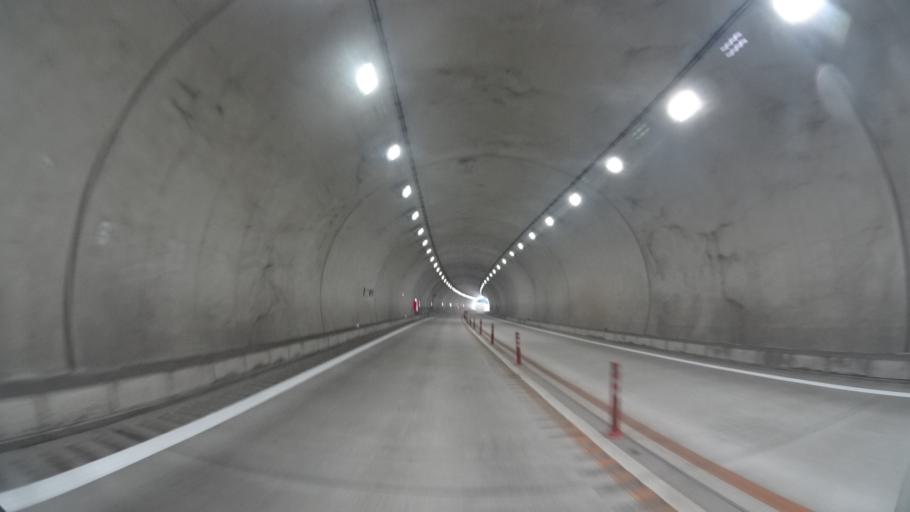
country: JP
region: Shimane
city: Odacho-oda
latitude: 35.1100
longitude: 132.3835
